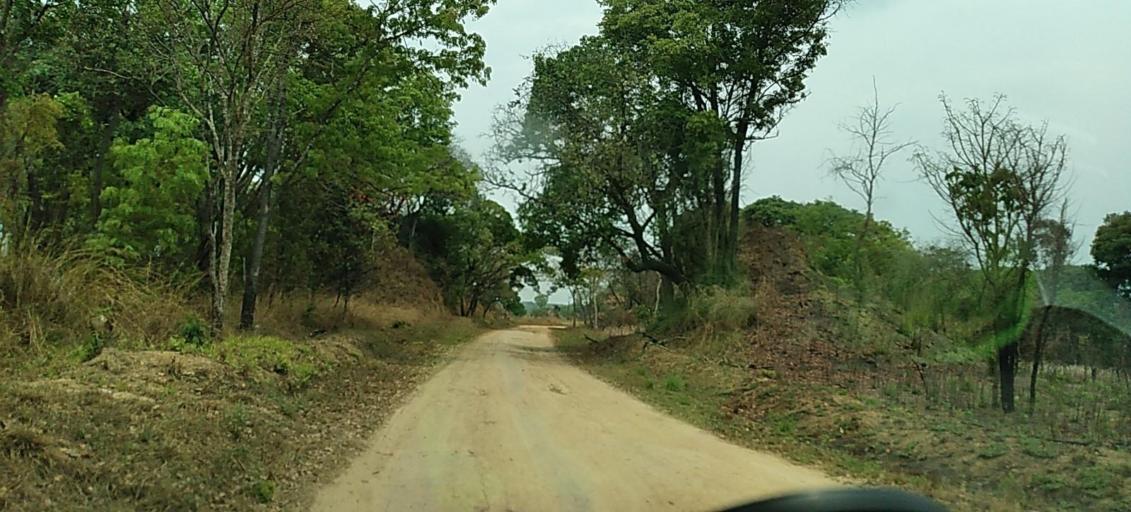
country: ZM
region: North-Western
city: Solwezi
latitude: -12.7875
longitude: 26.5266
